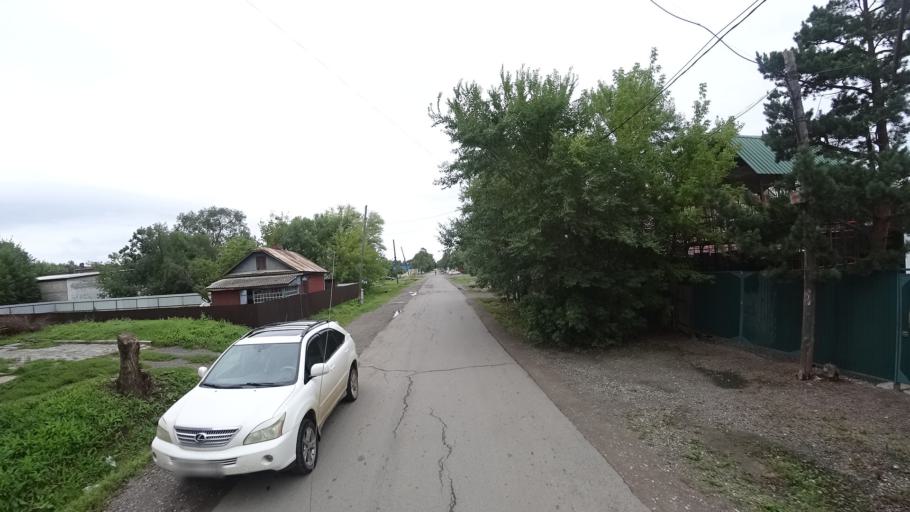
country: RU
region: Primorskiy
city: Chernigovka
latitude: 44.3457
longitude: 132.5739
